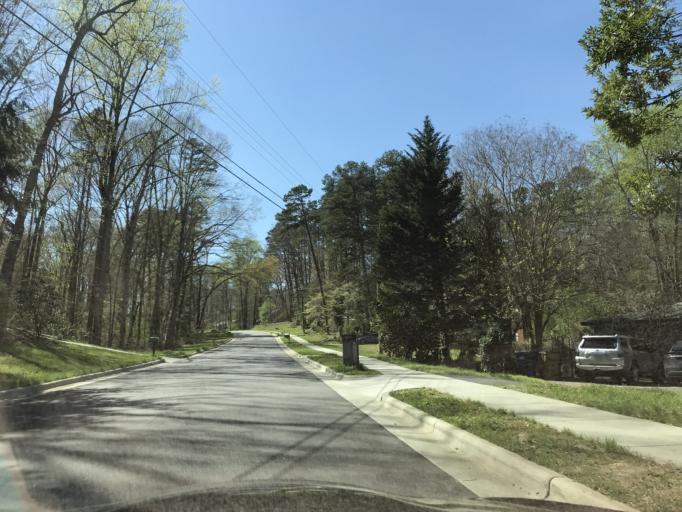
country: US
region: North Carolina
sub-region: Wake County
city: West Raleigh
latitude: 35.7799
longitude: -78.6993
